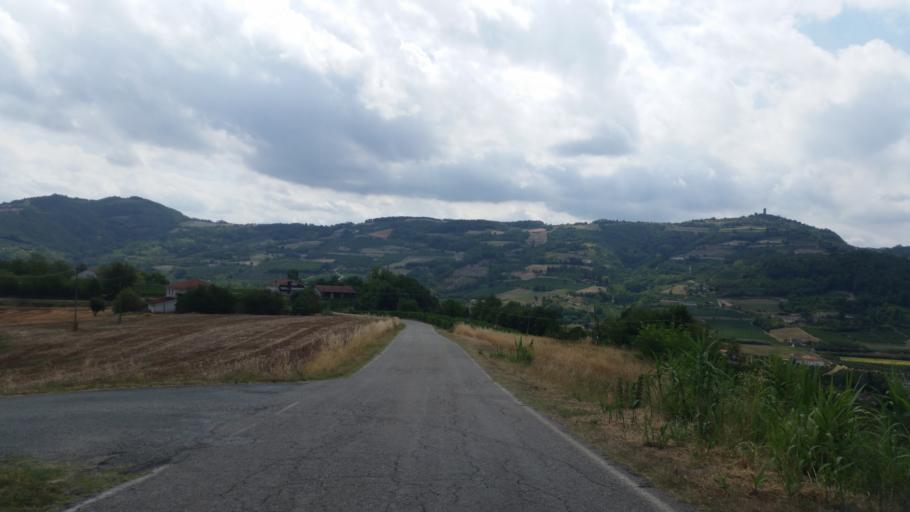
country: IT
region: Piedmont
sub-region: Provincia di Asti
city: Vesime
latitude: 44.6402
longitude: 8.2307
